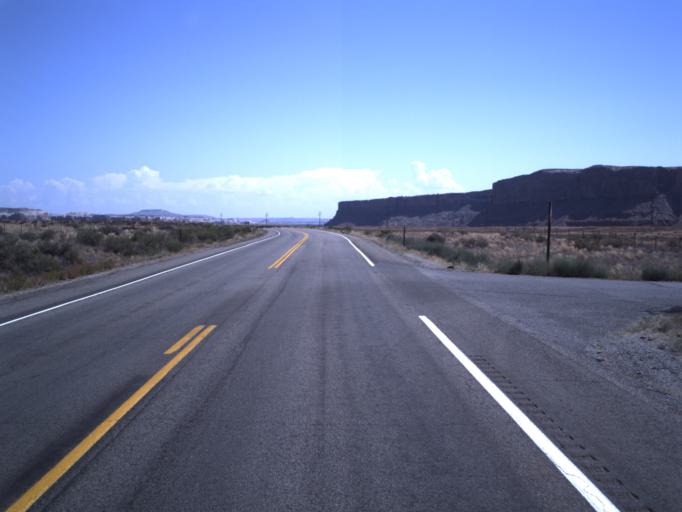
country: US
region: Utah
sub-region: San Juan County
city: Blanding
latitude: 37.2669
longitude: -109.6110
